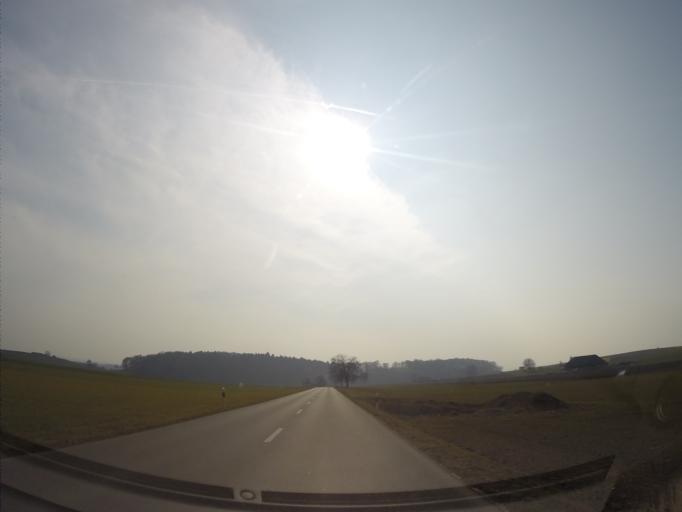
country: CH
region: Zurich
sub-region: Bezirk Andelfingen
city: Kleinandelfingen
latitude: 47.6415
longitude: 8.7085
